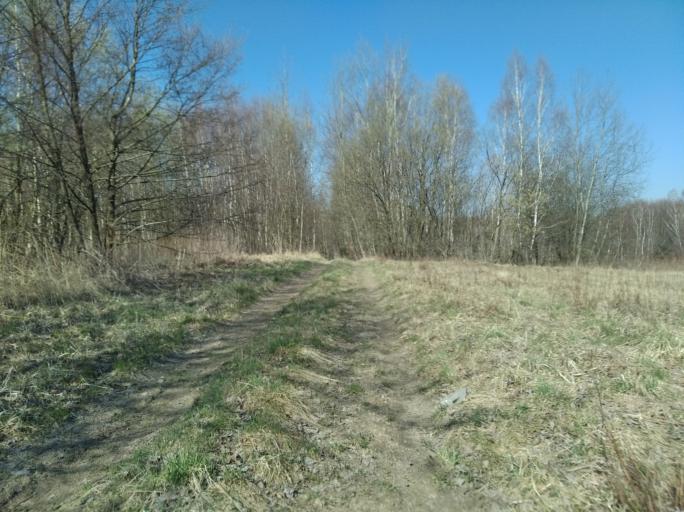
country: PL
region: Subcarpathian Voivodeship
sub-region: Powiat strzyzowski
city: Jawornik
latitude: 49.8526
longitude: 21.8541
